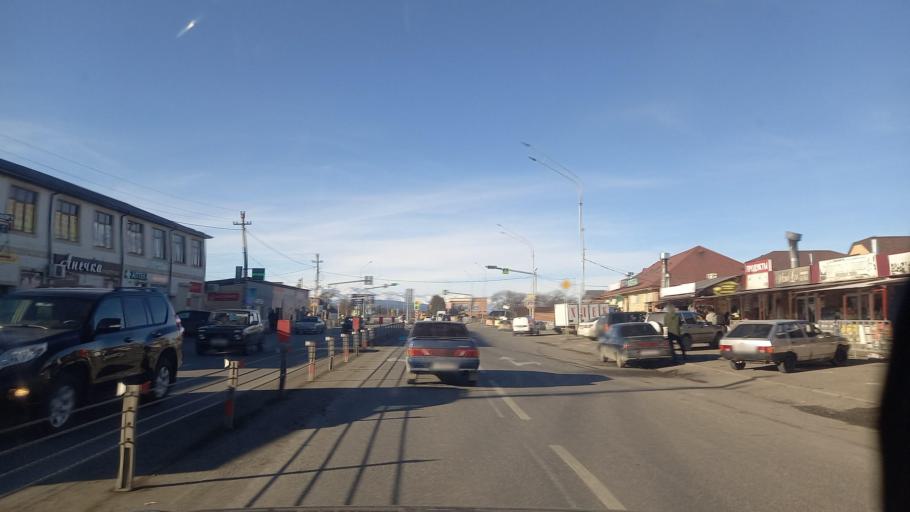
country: RU
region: North Ossetia
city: Gizel'
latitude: 43.0248
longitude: 44.5702
